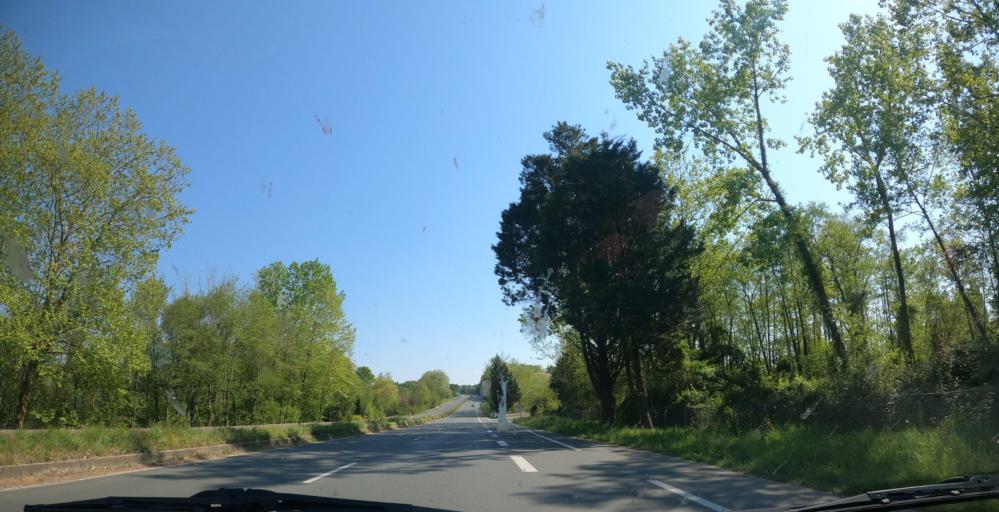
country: FR
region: Aquitaine
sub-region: Departement des Pyrenees-Atlantiques
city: Bassussarry
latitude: 43.4518
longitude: -1.4936
